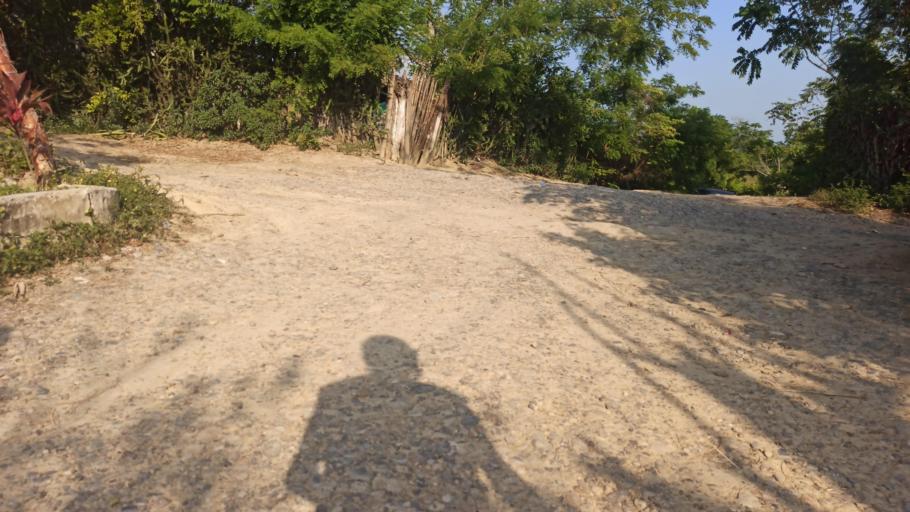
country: MX
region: Veracruz
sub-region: Papantla
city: Polutla
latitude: 20.6021
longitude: -97.2594
